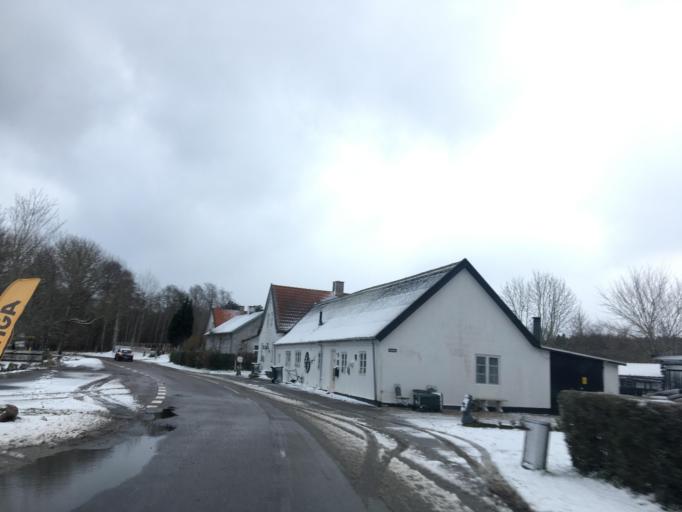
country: DK
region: Zealand
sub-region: Odsherred Kommune
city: Asnaes
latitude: 55.8306
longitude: 11.5663
